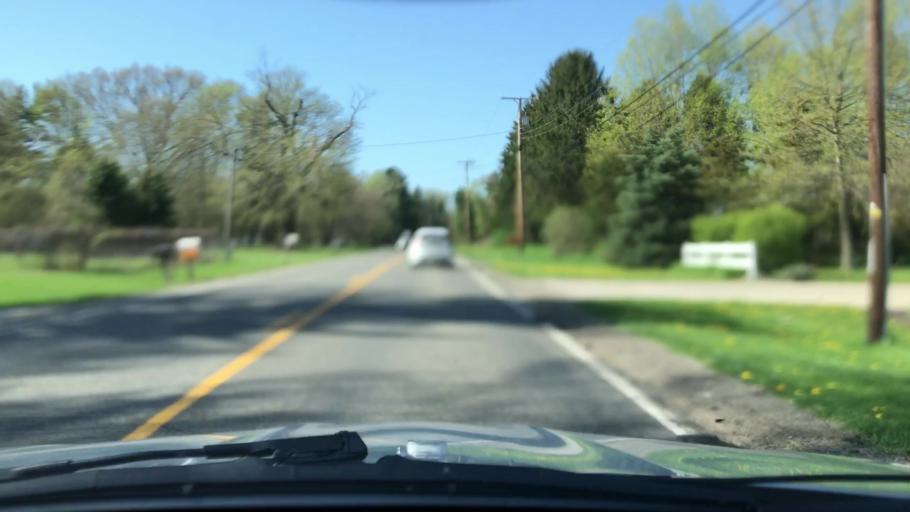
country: US
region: Indiana
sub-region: Saint Joseph County
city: Georgetown
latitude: 41.7555
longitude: -86.3028
